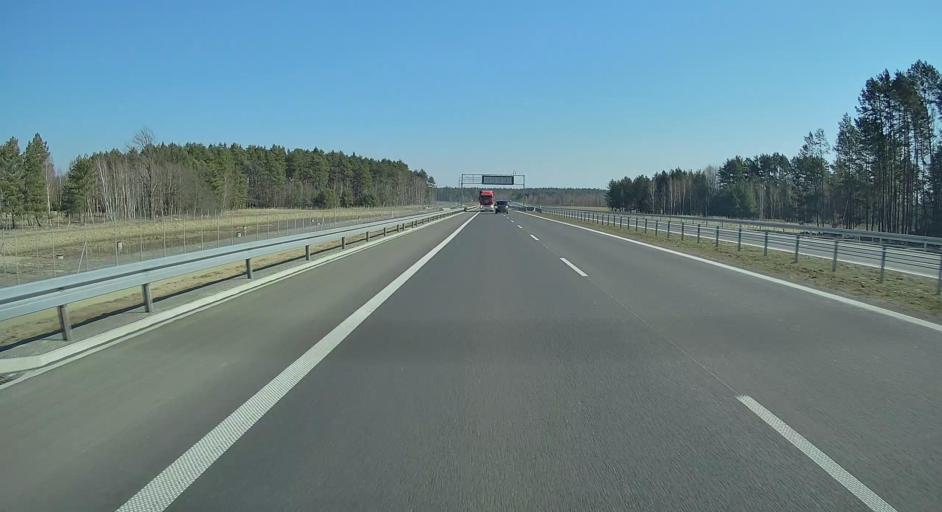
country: PL
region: Subcarpathian Voivodeship
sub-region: Powiat nizanski
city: Raclawice
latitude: 50.4741
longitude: 22.1662
